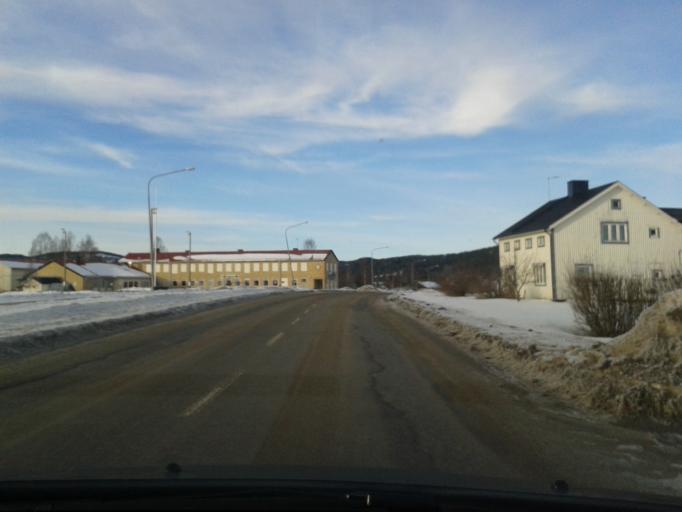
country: SE
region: Vaesternorrland
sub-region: OErnskoeldsviks Kommun
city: Bredbyn
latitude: 63.5117
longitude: 18.0650
